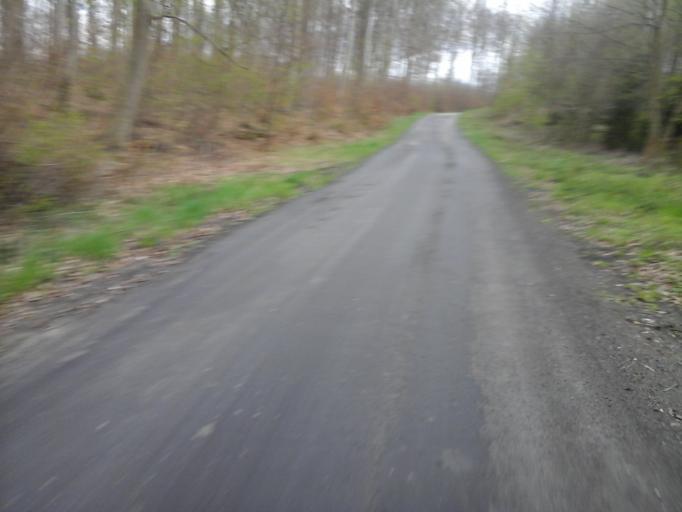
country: PL
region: West Pomeranian Voivodeship
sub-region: Powiat choszczenski
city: Bierzwnik
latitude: 53.0680
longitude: 15.5845
